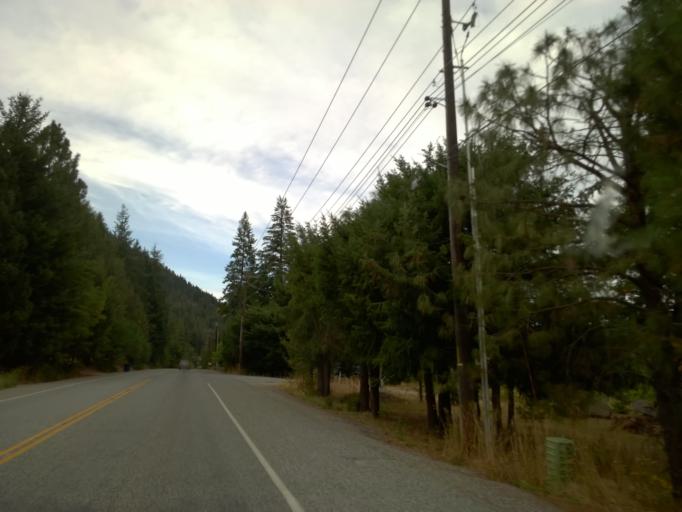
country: US
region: Washington
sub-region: Chelan County
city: Leavenworth
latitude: 47.5659
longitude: -120.6797
